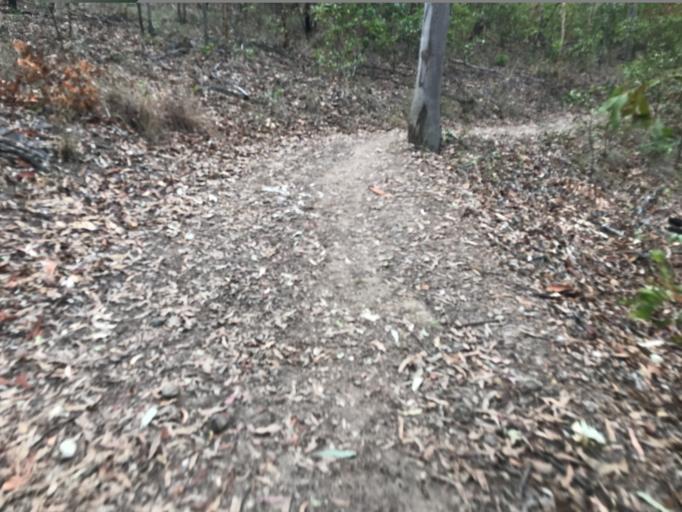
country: AU
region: Queensland
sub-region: Brisbane
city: Taringa
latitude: -27.4708
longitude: 152.9510
